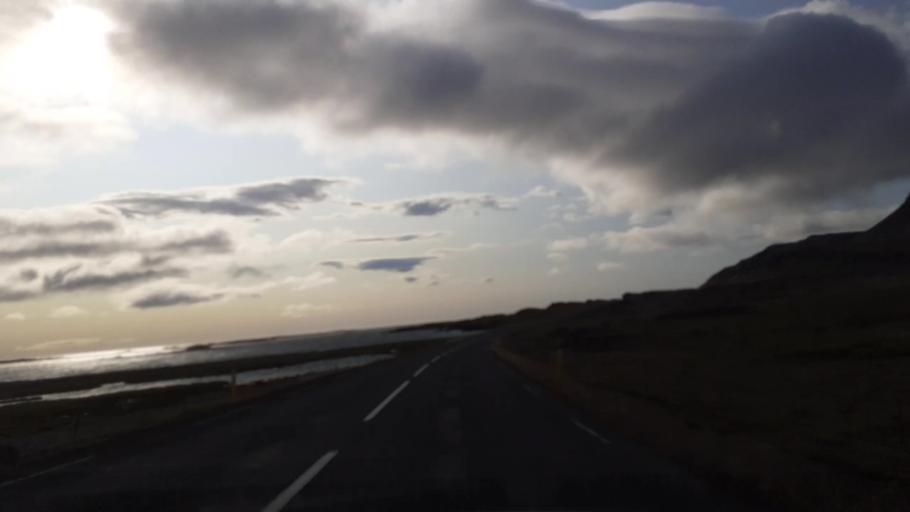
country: IS
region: East
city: Eskifjoerdur
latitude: 64.7577
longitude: -14.0247
